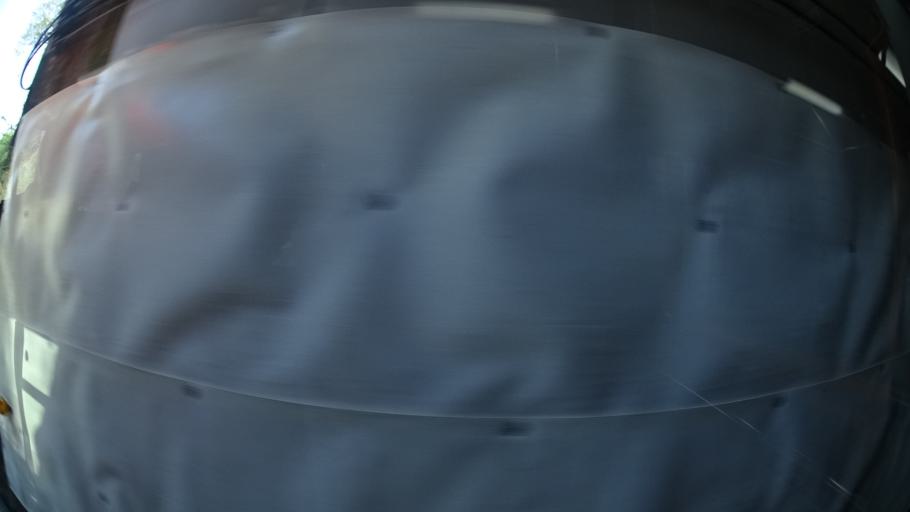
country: JP
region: Iwate
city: Ofunato
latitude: 38.9119
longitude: 141.5769
